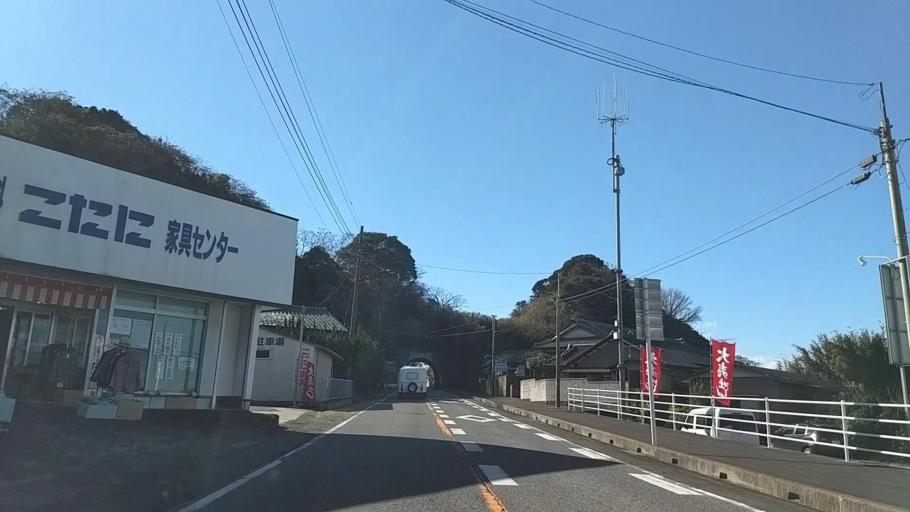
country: JP
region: Chiba
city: Tateyama
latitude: 34.9233
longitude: 139.8303
